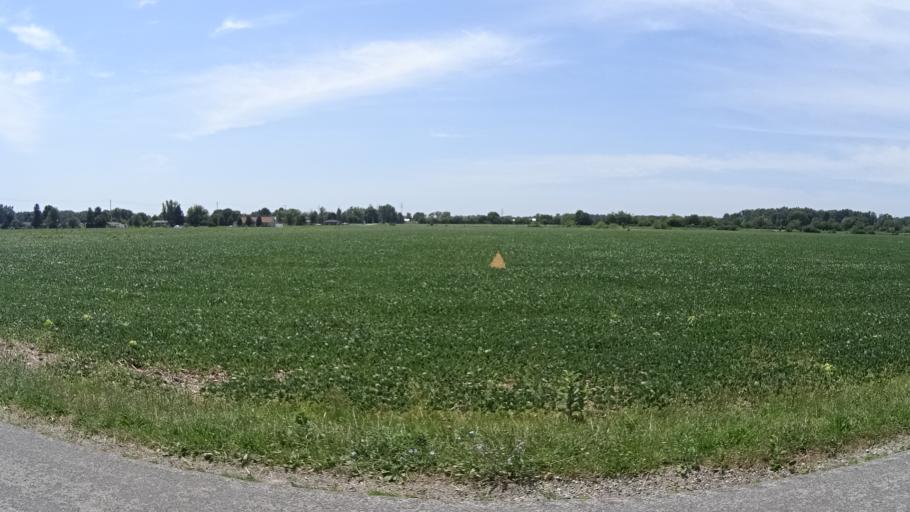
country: US
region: Ohio
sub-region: Erie County
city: Sandusky
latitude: 41.3623
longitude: -82.7697
